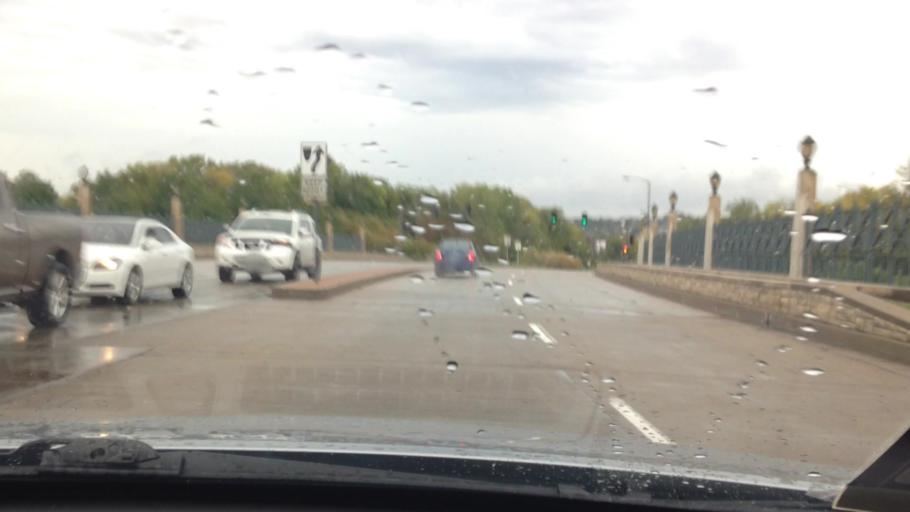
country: US
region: Missouri
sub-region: Jackson County
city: Kansas City
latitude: 39.0827
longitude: -94.5664
